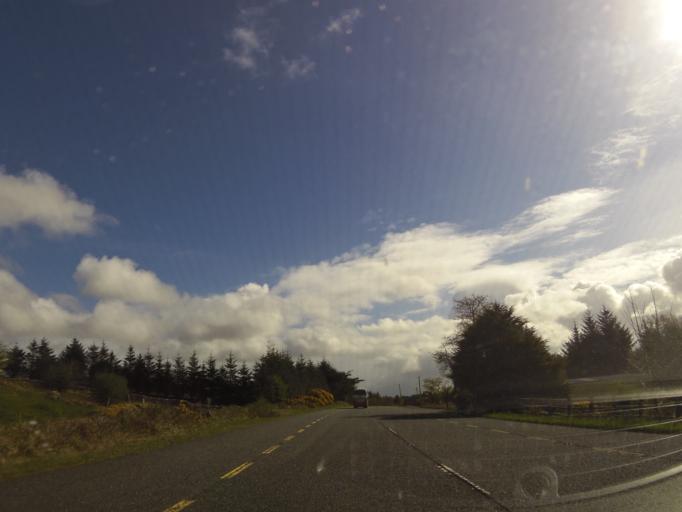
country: IE
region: Connaught
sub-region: Maigh Eo
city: Ballyhaunis
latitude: 53.8791
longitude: -8.8271
